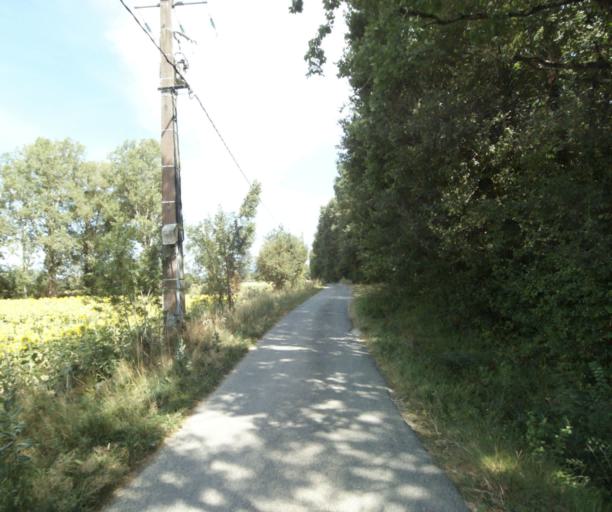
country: FR
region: Midi-Pyrenees
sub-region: Departement du Tarn
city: Puylaurens
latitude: 43.5146
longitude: 2.0407
